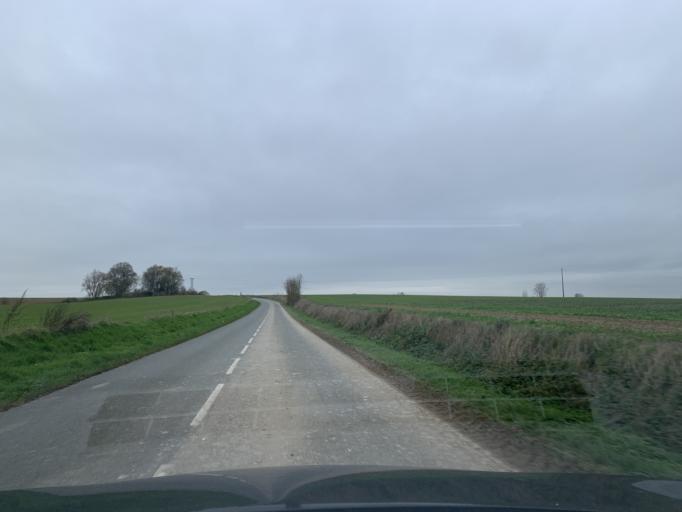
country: FR
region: Nord-Pas-de-Calais
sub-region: Departement du Pas-de-Calais
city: Oisy-le-Verger
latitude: 50.2430
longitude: 3.1383
